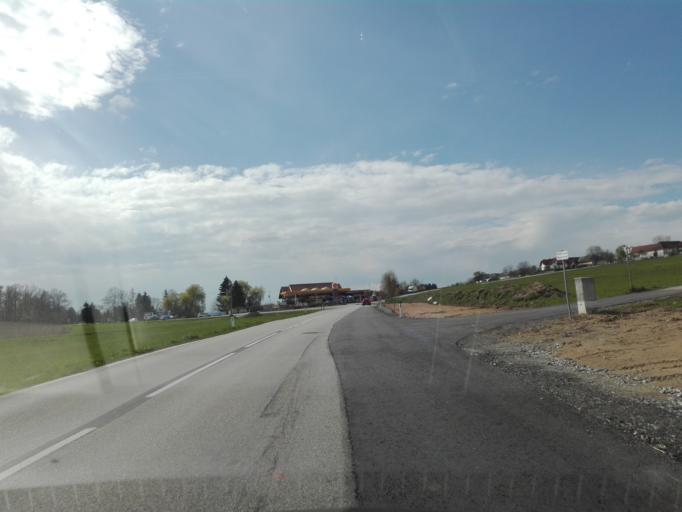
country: AT
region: Upper Austria
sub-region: Politischer Bezirk Rohrbach
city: Kleinzell im Muehlkreis
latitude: 48.4377
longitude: 14.0395
